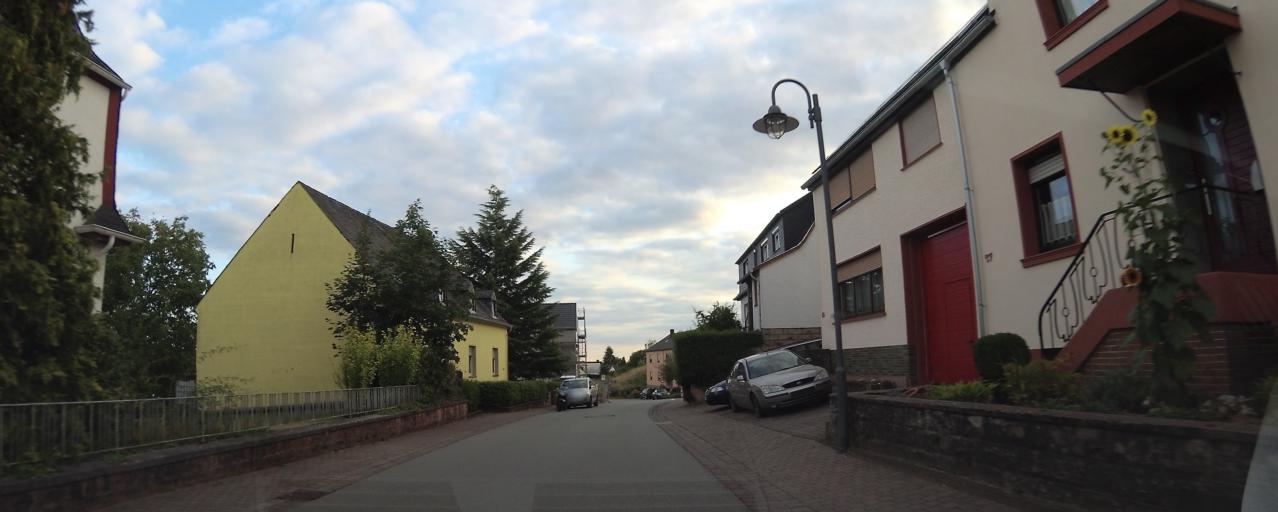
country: DE
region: Rheinland-Pfalz
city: Fohren
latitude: 49.8636
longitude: 6.7699
